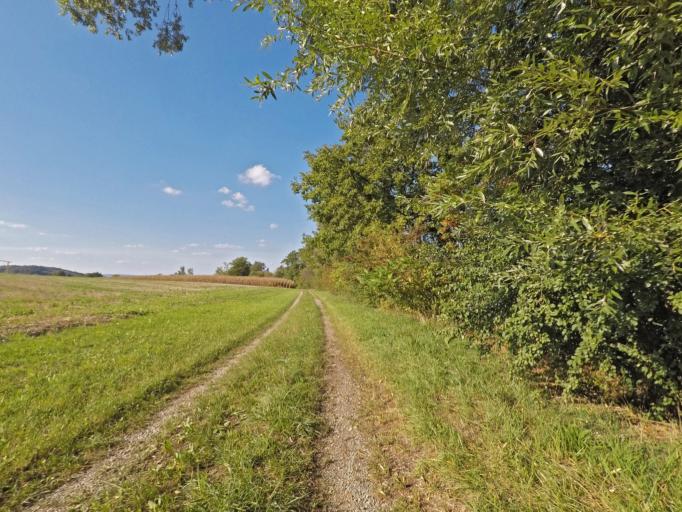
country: CH
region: Thurgau
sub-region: Frauenfeld District
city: Diessenhofen
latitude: 47.6619
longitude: 8.7473
